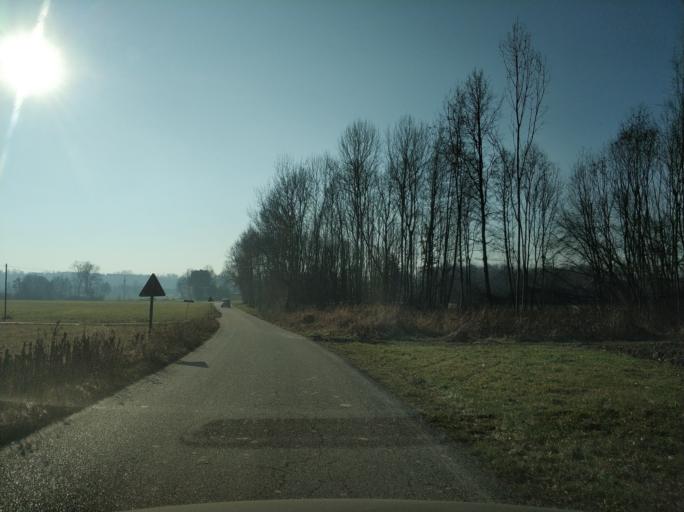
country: IT
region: Piedmont
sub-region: Provincia di Torino
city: Levone
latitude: 45.3050
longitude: 7.6154
